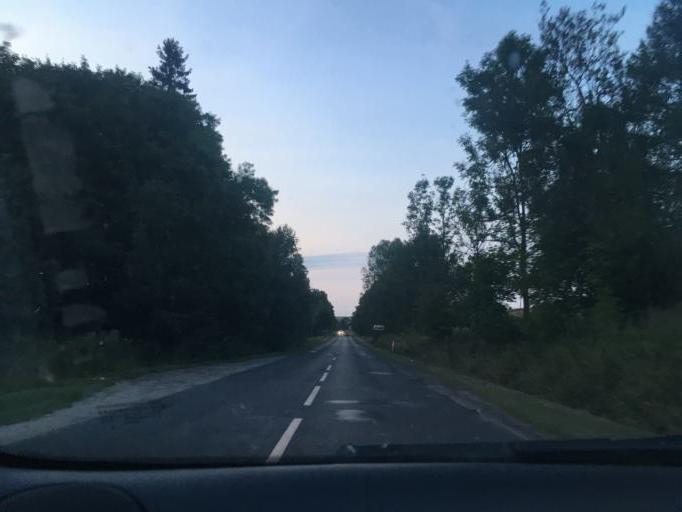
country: PL
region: Lower Silesian Voivodeship
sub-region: Powiat walbrzyski
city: Czarny Bor
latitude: 50.7678
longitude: 16.1595
